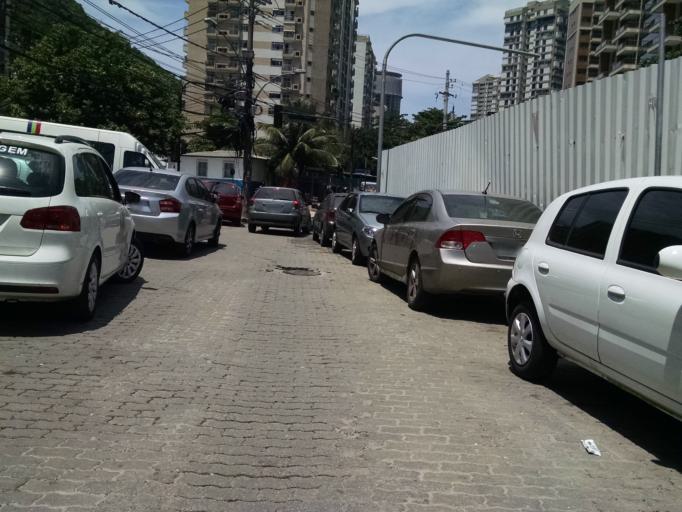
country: BR
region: Rio de Janeiro
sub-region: Rio De Janeiro
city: Rio de Janeiro
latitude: -22.9933
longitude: -43.2529
